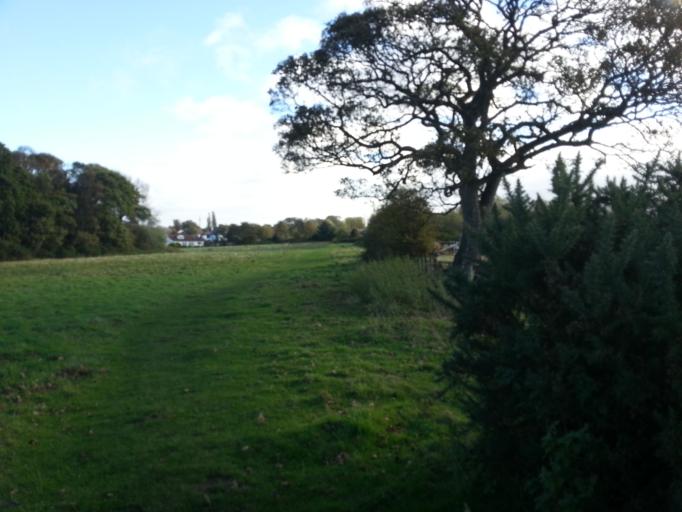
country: GB
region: England
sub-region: Metropolitan Borough of Wirral
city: Heswall
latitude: 53.3506
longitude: -3.1285
